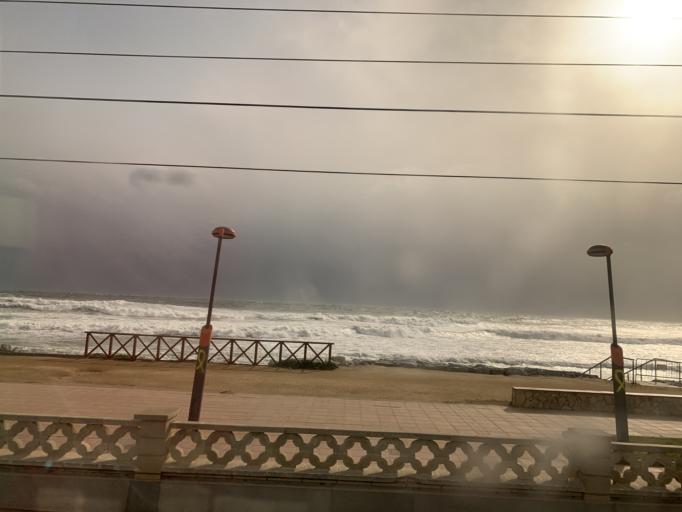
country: ES
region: Catalonia
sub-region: Provincia de Barcelona
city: Vilassar de Mar
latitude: 41.5037
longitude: 2.3959
